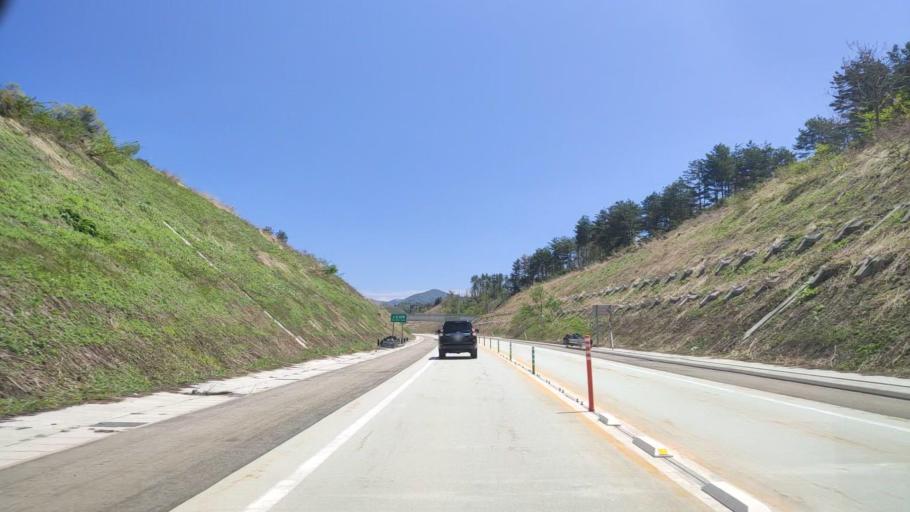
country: JP
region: Yamagata
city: Obanazawa
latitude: 38.5893
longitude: 140.3897
